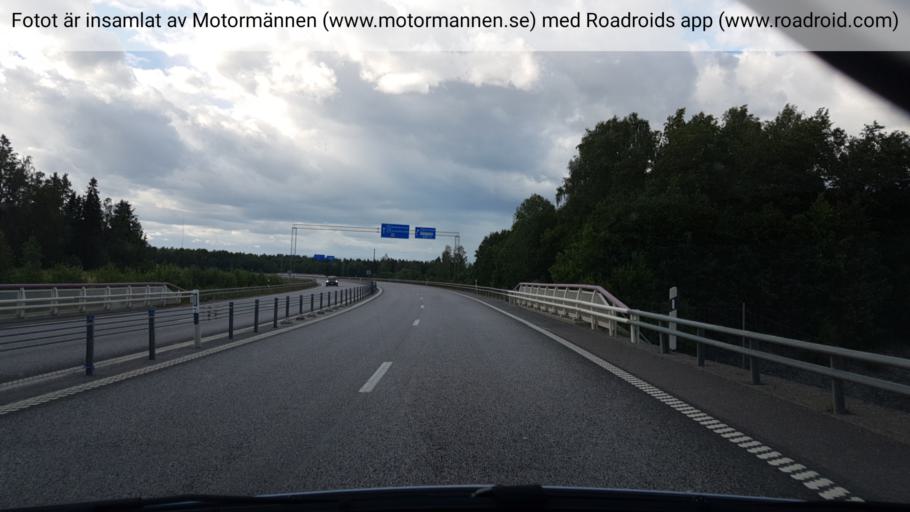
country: SE
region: Vaestra Goetaland
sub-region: Skovde Kommun
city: Skultorp
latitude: 58.3589
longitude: 13.8654
